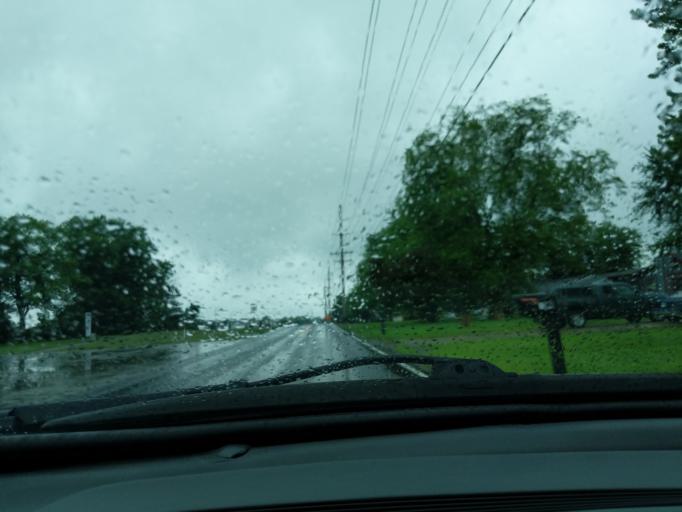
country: US
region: Indiana
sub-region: Hamilton County
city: Noblesville
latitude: 40.0748
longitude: -86.0334
